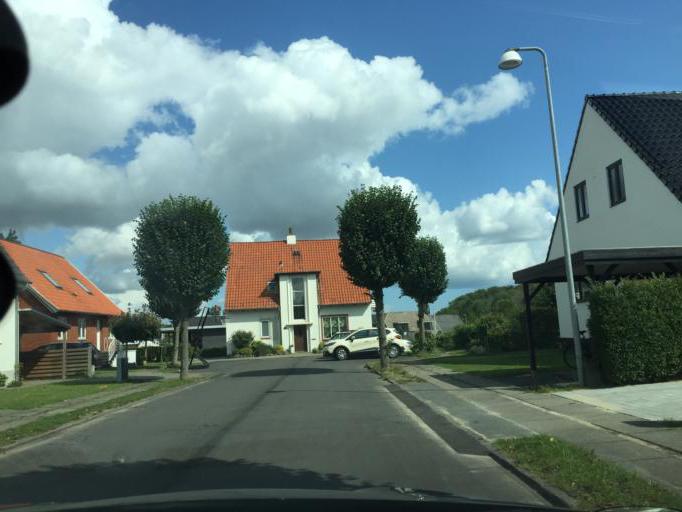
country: DK
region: South Denmark
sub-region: Odense Kommune
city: Odense
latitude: 55.4022
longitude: 10.3552
